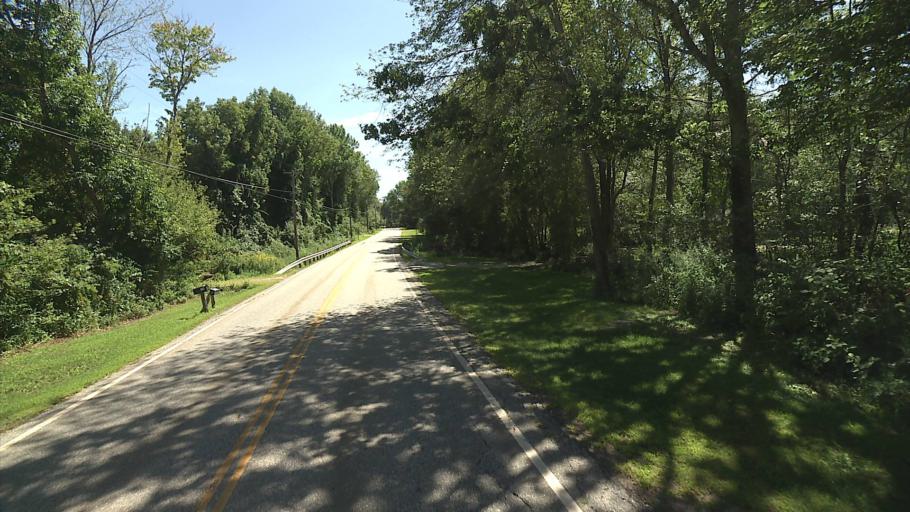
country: US
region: Connecticut
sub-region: Windham County
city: Windham
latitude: 41.7105
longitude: -72.0676
